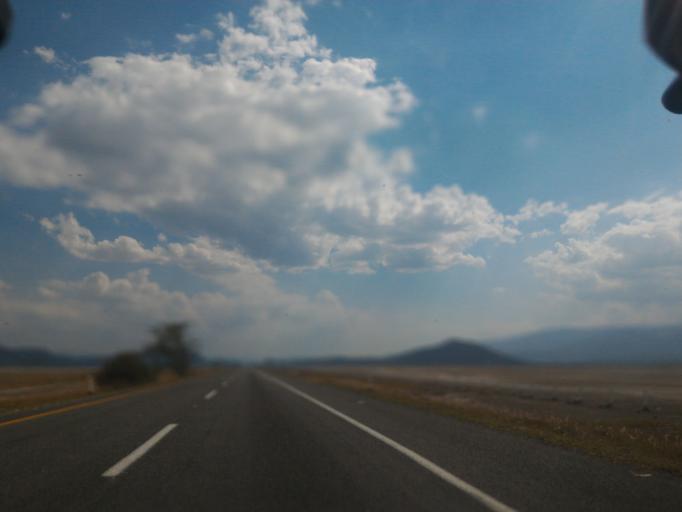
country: MX
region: Jalisco
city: Zacoalco de Torres
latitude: 20.3105
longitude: -103.5621
